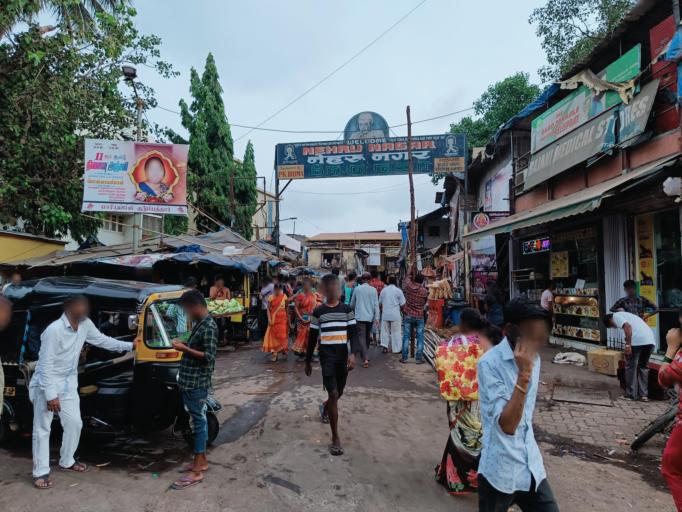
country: IN
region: Maharashtra
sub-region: Mumbai Suburban
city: Mumbai
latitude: 19.1037
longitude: 72.8313
